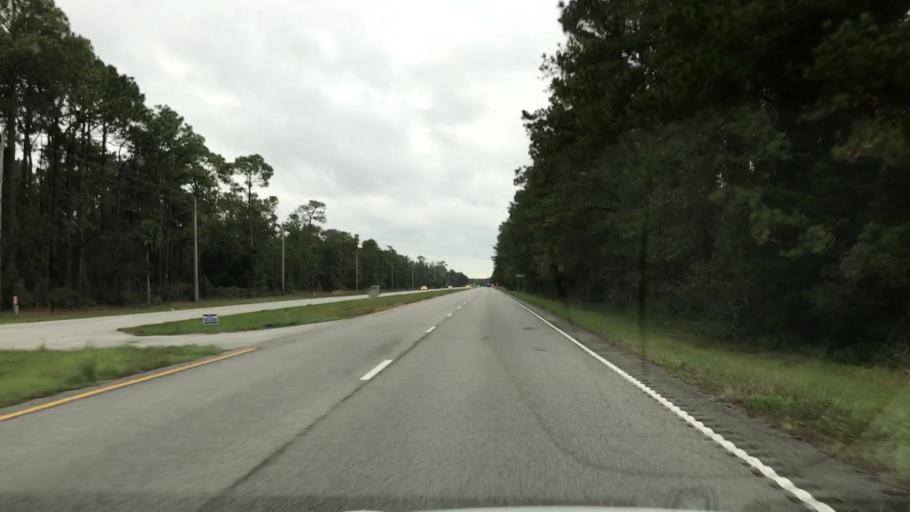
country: US
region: South Carolina
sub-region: Georgetown County
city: Georgetown
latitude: 33.3708
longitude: -79.2180
